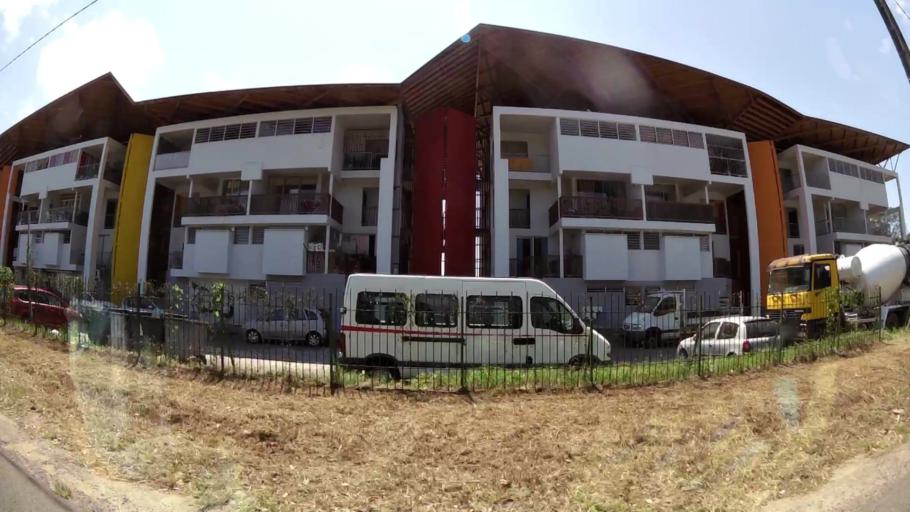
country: GF
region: Guyane
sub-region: Guyane
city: Cayenne
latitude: 4.9197
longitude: -52.3218
